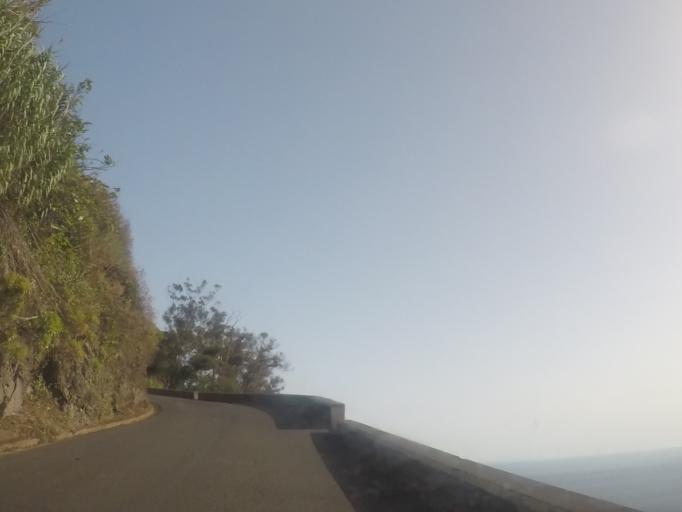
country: PT
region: Madeira
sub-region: Calheta
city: Arco da Calheta
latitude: 32.7095
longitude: -17.1303
